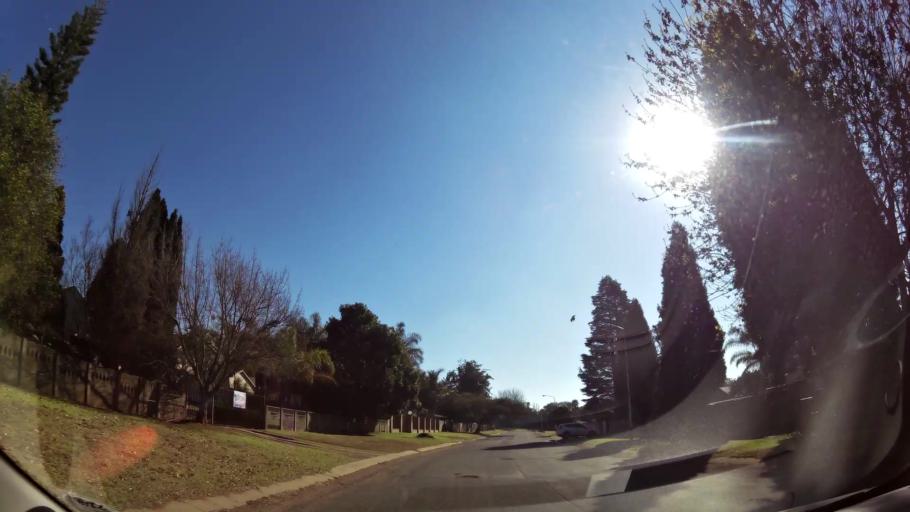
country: ZA
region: Mpumalanga
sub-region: Nkangala District Municipality
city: Witbank
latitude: -25.8830
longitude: 29.2373
